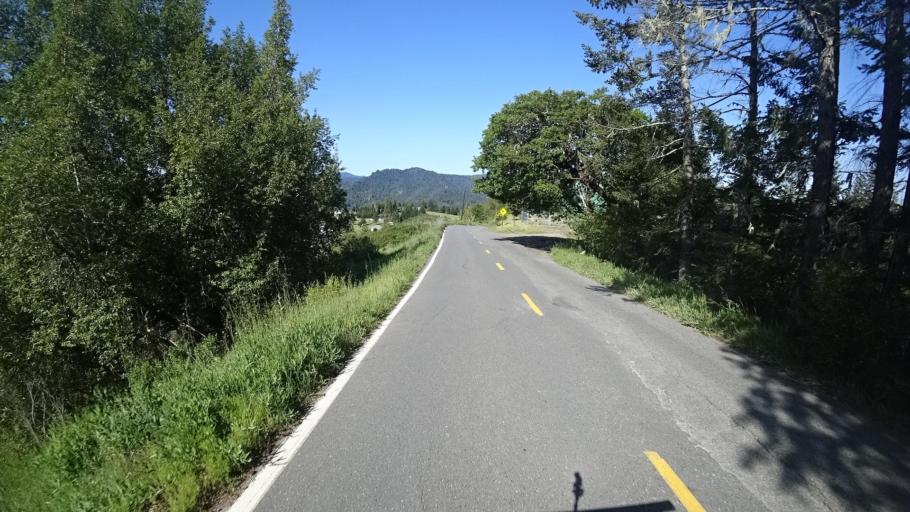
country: US
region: California
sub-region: Humboldt County
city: Redway
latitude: 40.1106
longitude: -123.7806
